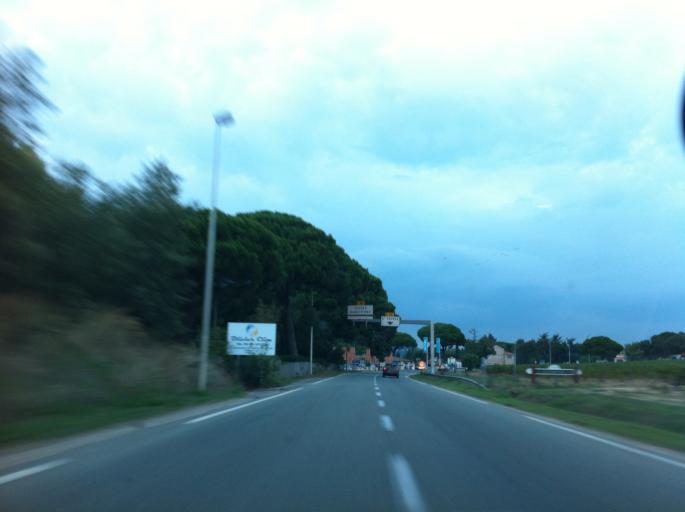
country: FR
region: Provence-Alpes-Cote d'Azur
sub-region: Departement du Var
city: Gassin
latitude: 43.2584
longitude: 6.5948
